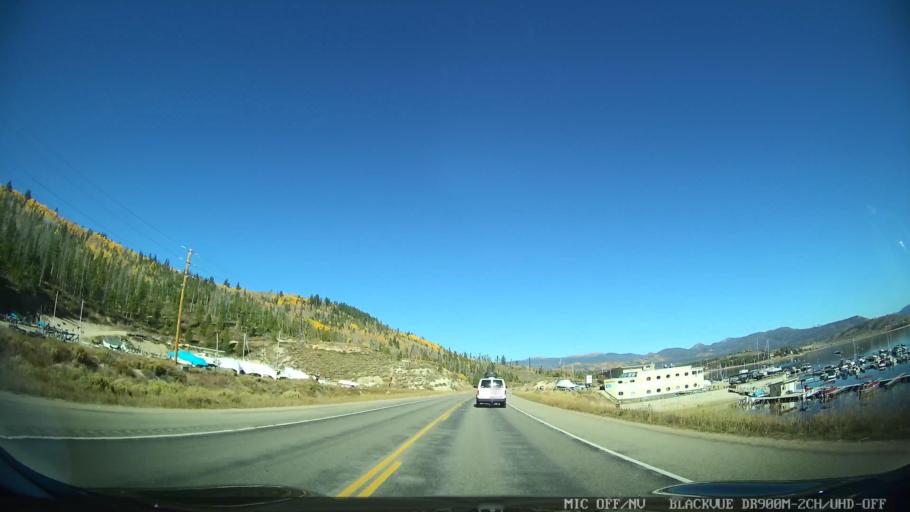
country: US
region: Colorado
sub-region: Grand County
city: Granby
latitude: 40.1595
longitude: -105.8929
